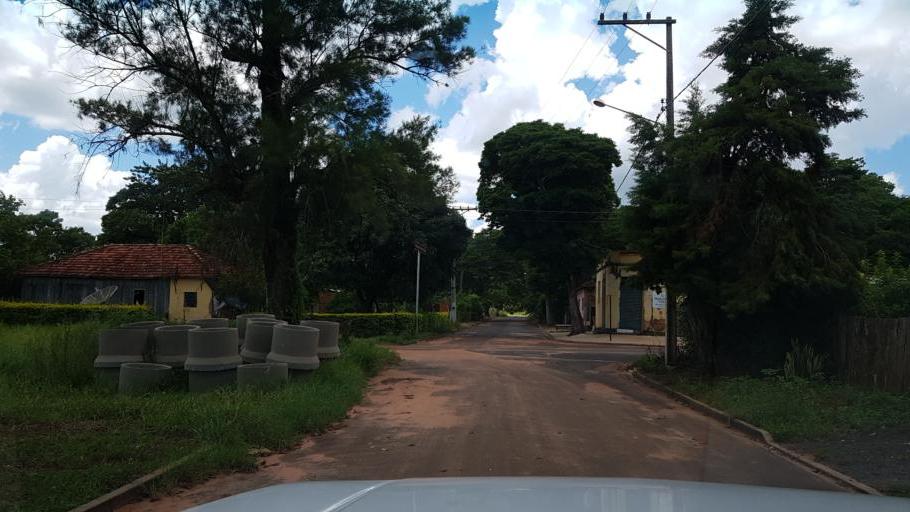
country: BR
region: Sao Paulo
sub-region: Paraguacu Paulista
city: Paraguacu Paulista
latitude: -22.3513
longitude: -50.6230
